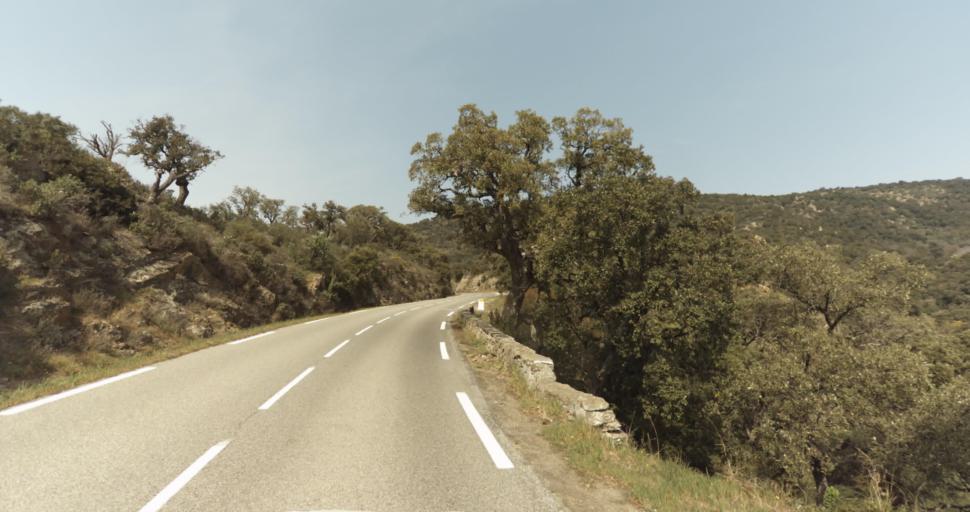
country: FR
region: Provence-Alpes-Cote d'Azur
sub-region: Departement du Var
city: Bormes-les-Mimosas
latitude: 43.1601
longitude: 6.3435
